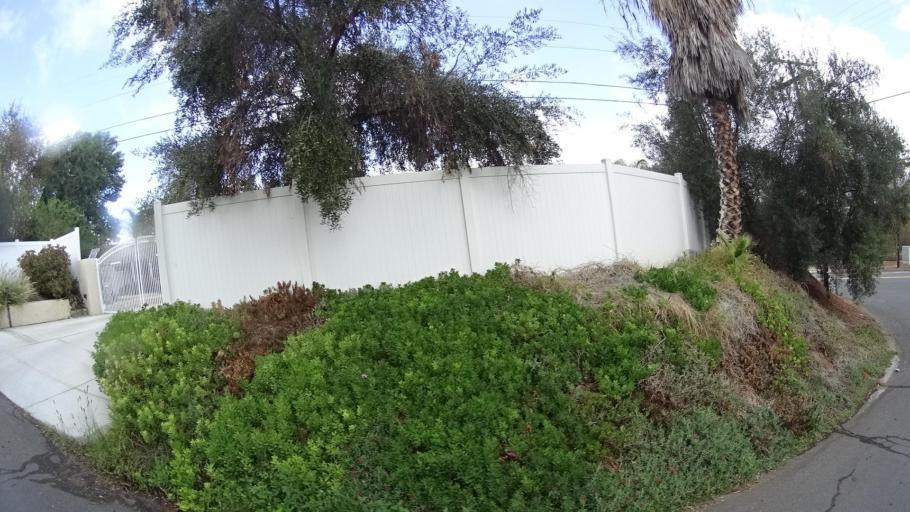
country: US
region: California
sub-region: San Diego County
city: Granite Hills
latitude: 32.7820
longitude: -116.9064
